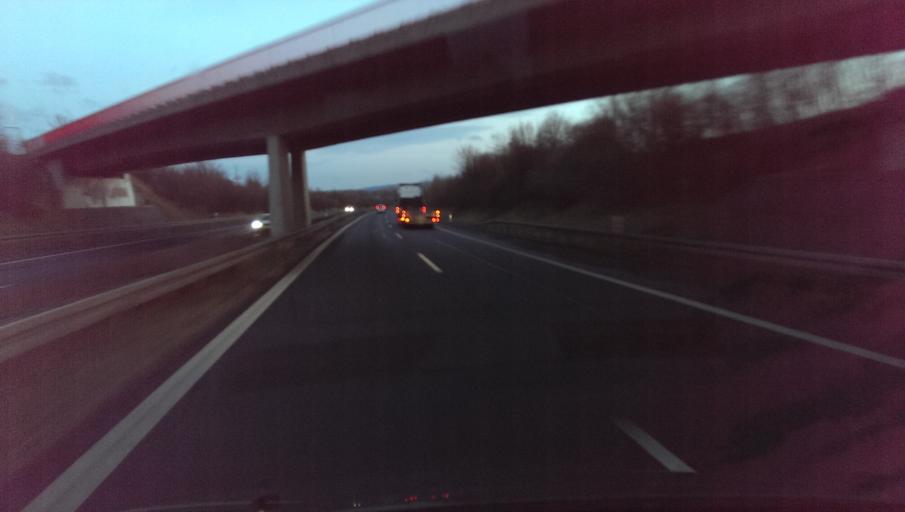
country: DE
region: Saxony-Anhalt
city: Veckenstedt
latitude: 51.8979
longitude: 10.7002
